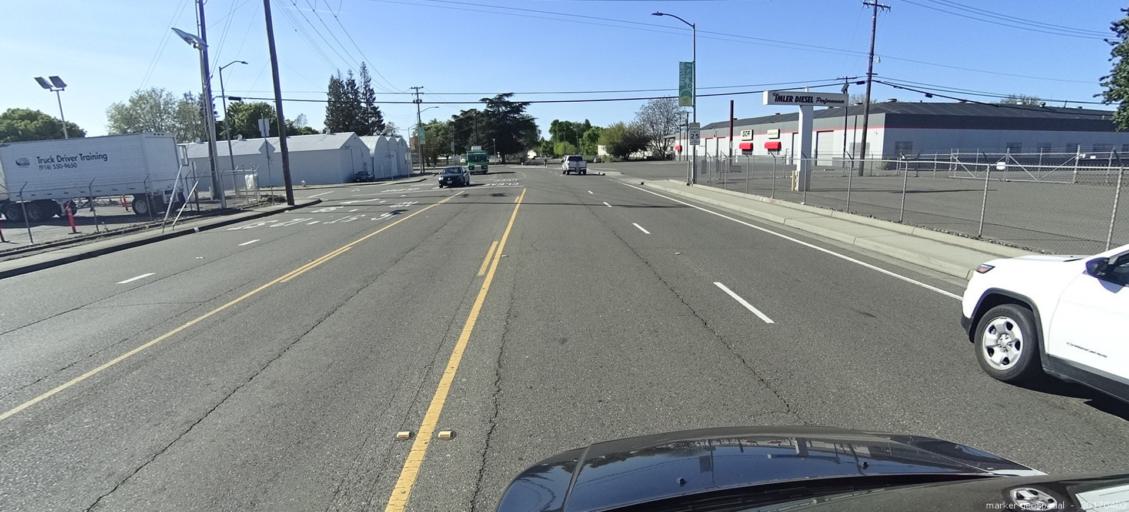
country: US
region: California
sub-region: Sacramento County
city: Sacramento
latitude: 38.5949
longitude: -121.4792
